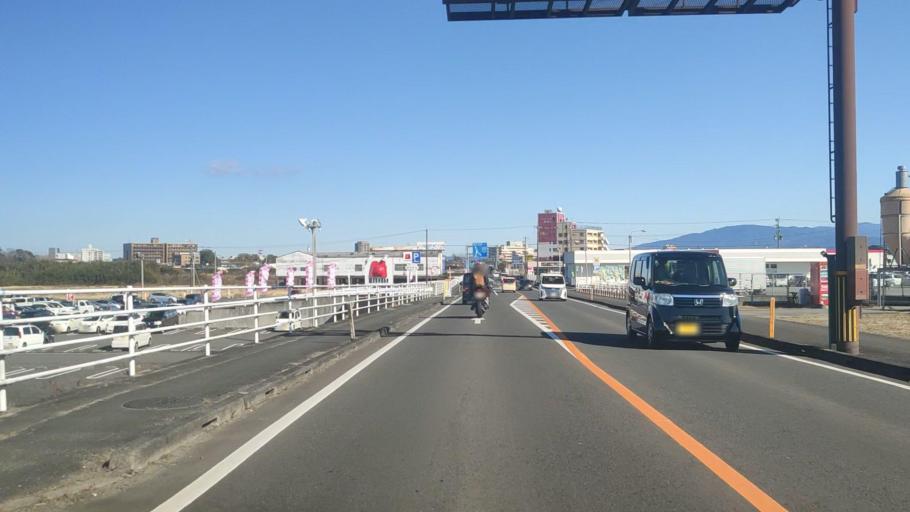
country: JP
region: Miyazaki
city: Miyakonojo
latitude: 31.7112
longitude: 131.0564
